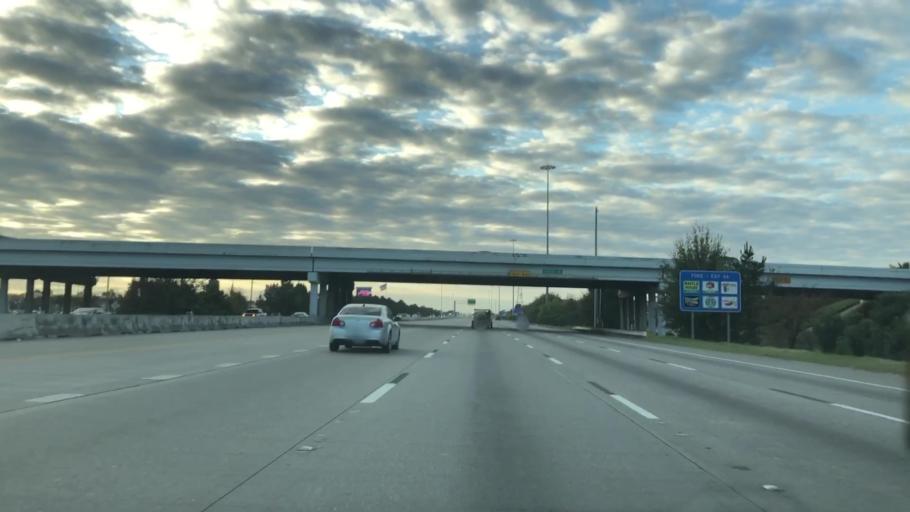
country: US
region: Texas
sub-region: Harris County
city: Spring
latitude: 30.0671
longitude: -95.4347
